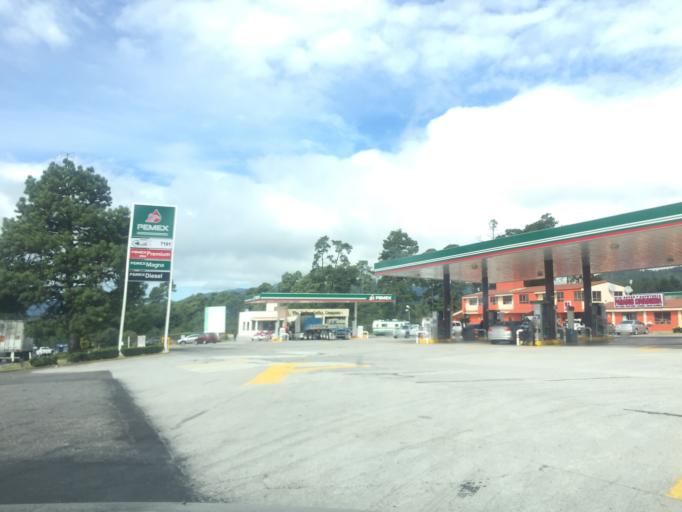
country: MX
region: Morelos
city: Tres Marias
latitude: 19.0845
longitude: -99.2242
